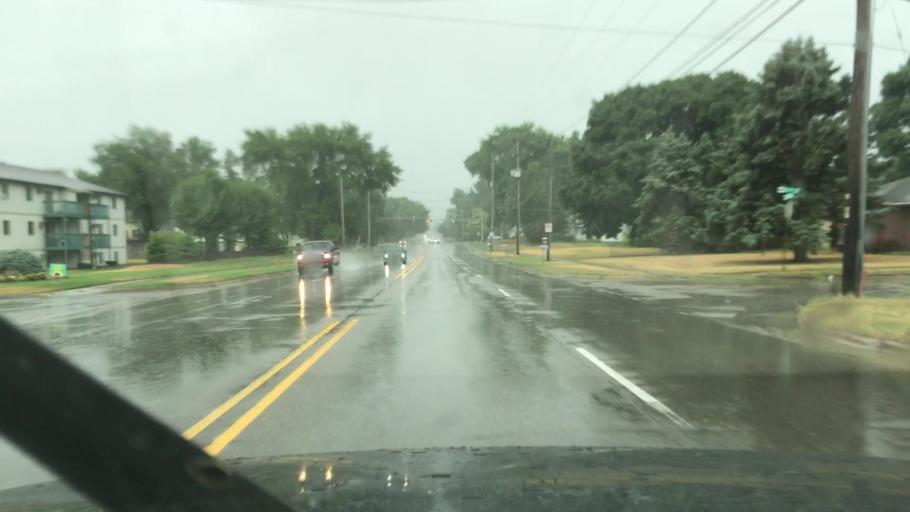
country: US
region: Michigan
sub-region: Kent County
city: Wyoming
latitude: 42.9086
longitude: -85.7248
